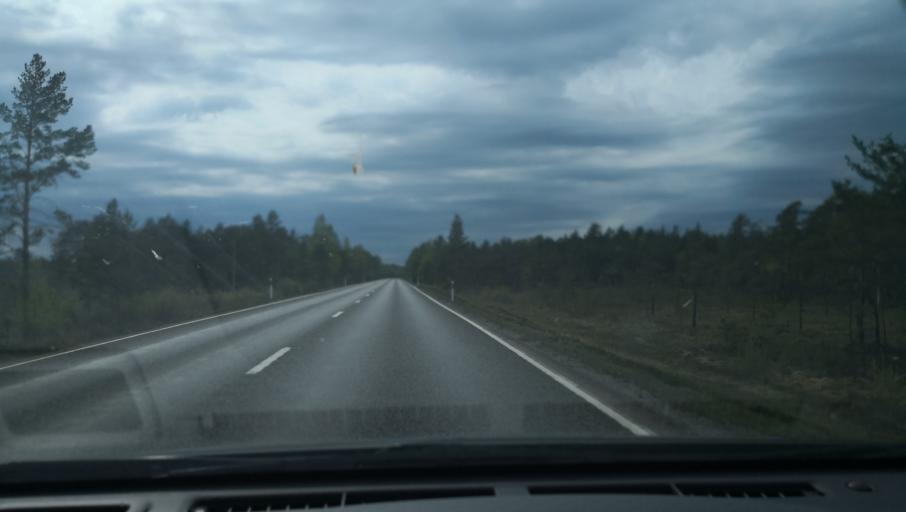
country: SE
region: Vaestmanland
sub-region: Skinnskattebergs Kommun
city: Skinnskatteberg
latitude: 59.8014
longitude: 15.7819
